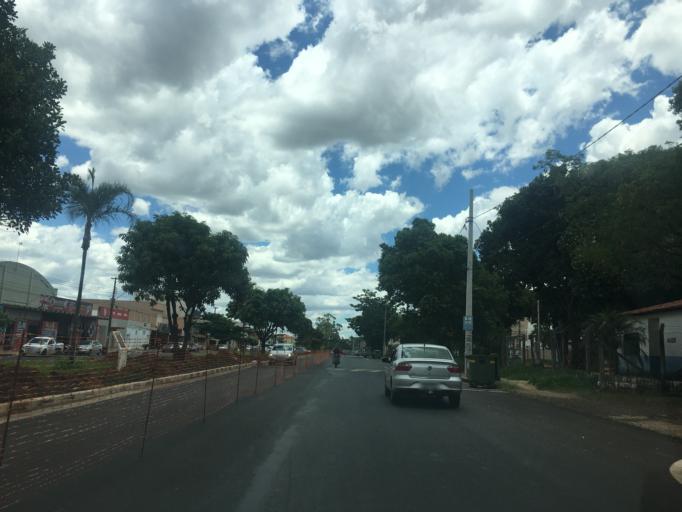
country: BR
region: Minas Gerais
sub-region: Uberlandia
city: Uberlandia
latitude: -18.9442
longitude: -48.3107
